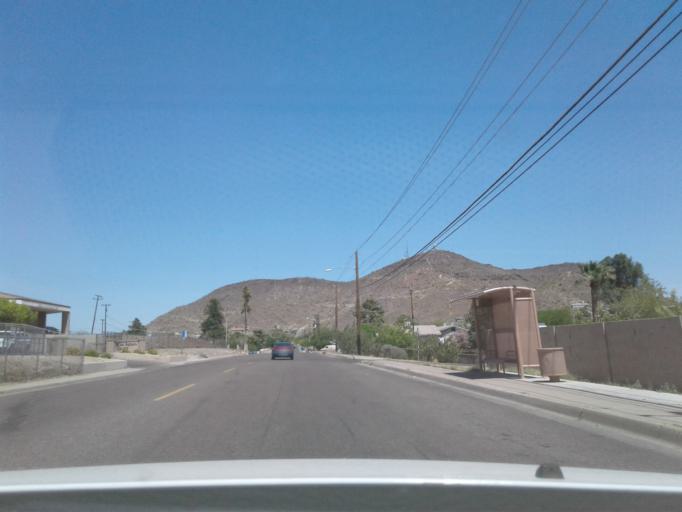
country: US
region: Arizona
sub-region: Maricopa County
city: Glendale
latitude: 33.5771
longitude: -112.0912
